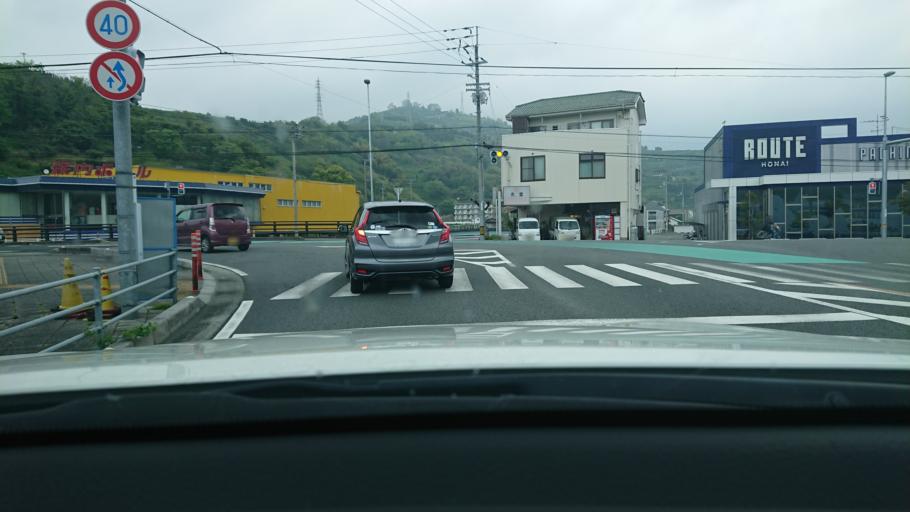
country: JP
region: Ehime
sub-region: Nishiuwa-gun
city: Ikata-cho
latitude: 33.4833
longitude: 132.4050
